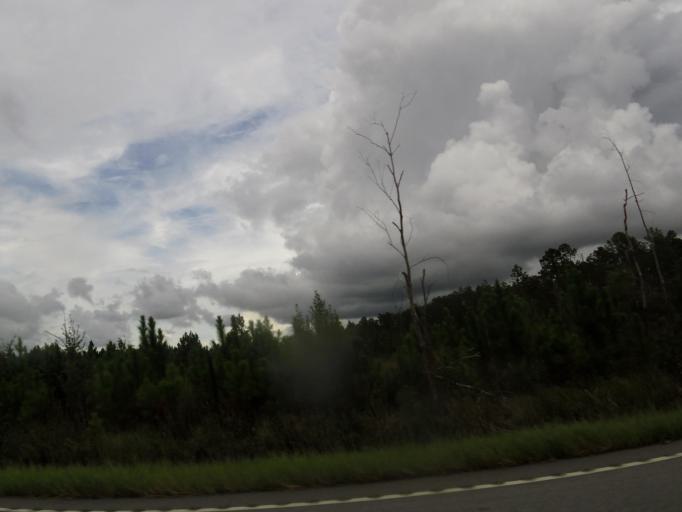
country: US
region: Florida
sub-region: Baker County
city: Macclenny
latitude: 30.5196
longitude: -82.1424
